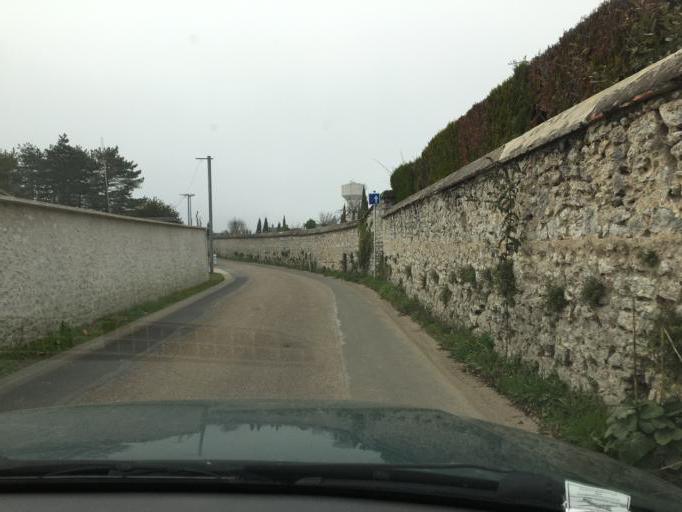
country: FR
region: Centre
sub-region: Departement du Loiret
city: Beaugency
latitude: 47.7827
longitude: 1.6368
